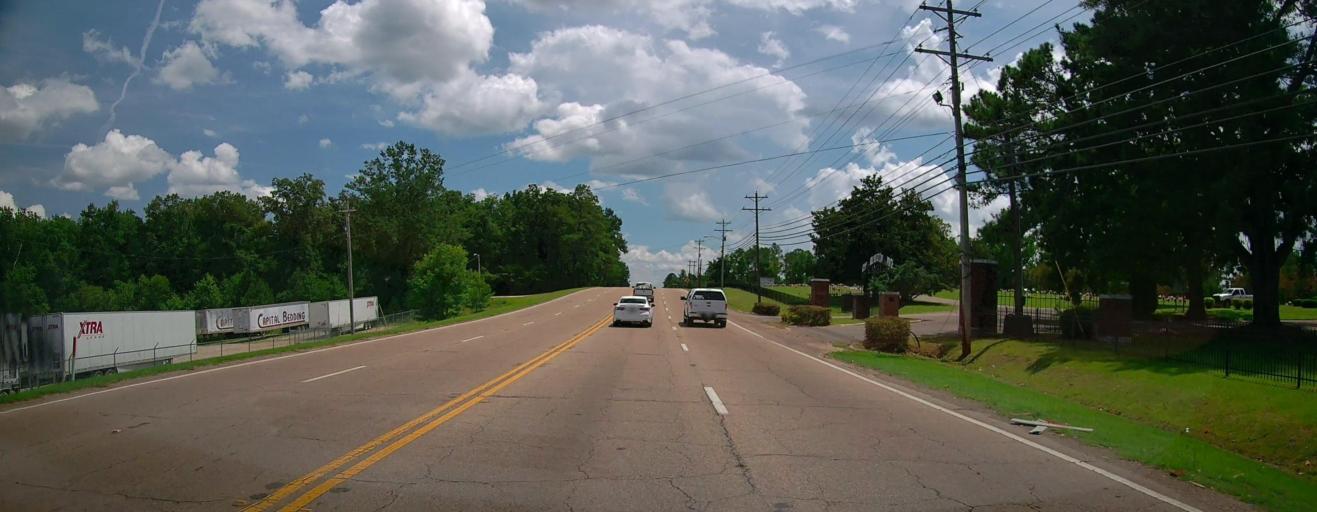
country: US
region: Mississippi
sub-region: Lee County
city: Verona
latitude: 34.1765
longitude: -88.7198
